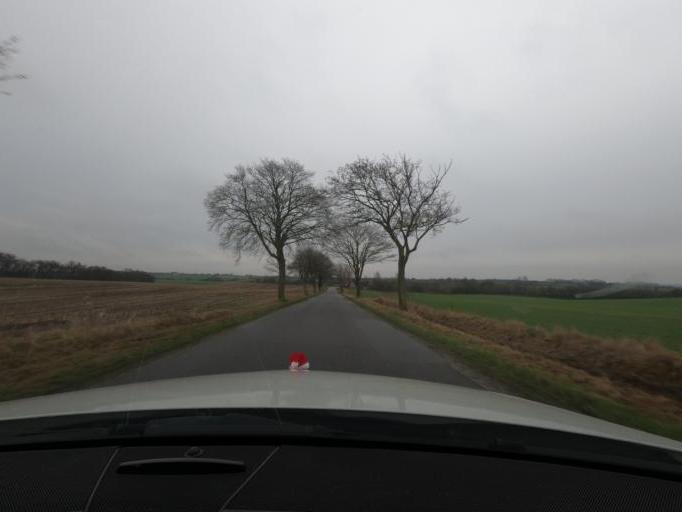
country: DK
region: South Denmark
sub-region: Haderslev Kommune
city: Haderslev
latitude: 55.1940
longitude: 9.4882
